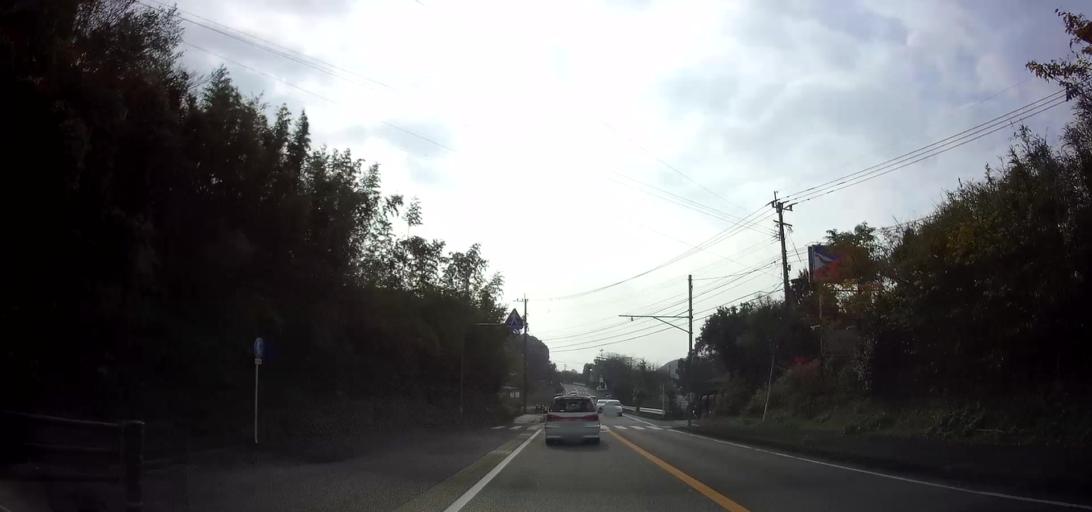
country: JP
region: Nagasaki
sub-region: Isahaya-shi
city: Isahaya
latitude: 32.7995
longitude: 130.1326
